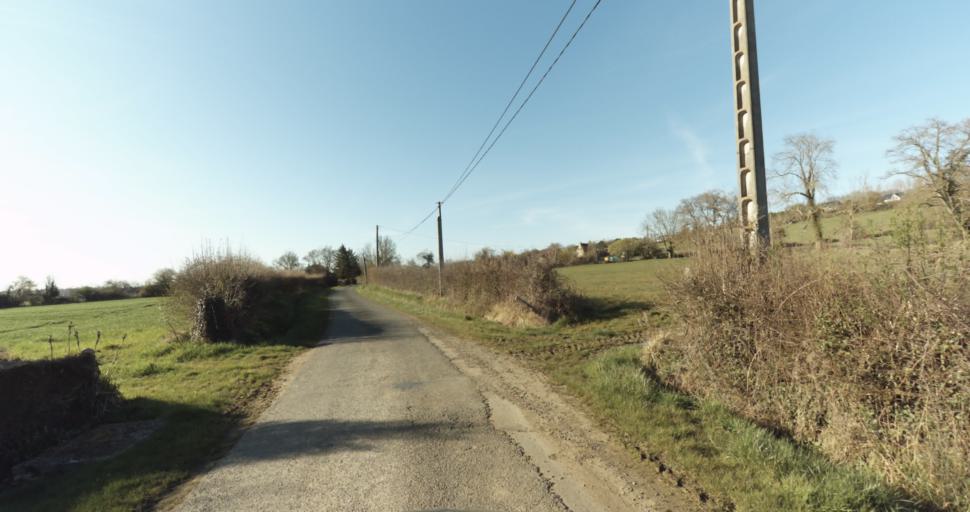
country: FR
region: Lower Normandy
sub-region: Departement du Calvados
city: Saint-Pierre-sur-Dives
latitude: 49.0470
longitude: 0.0256
